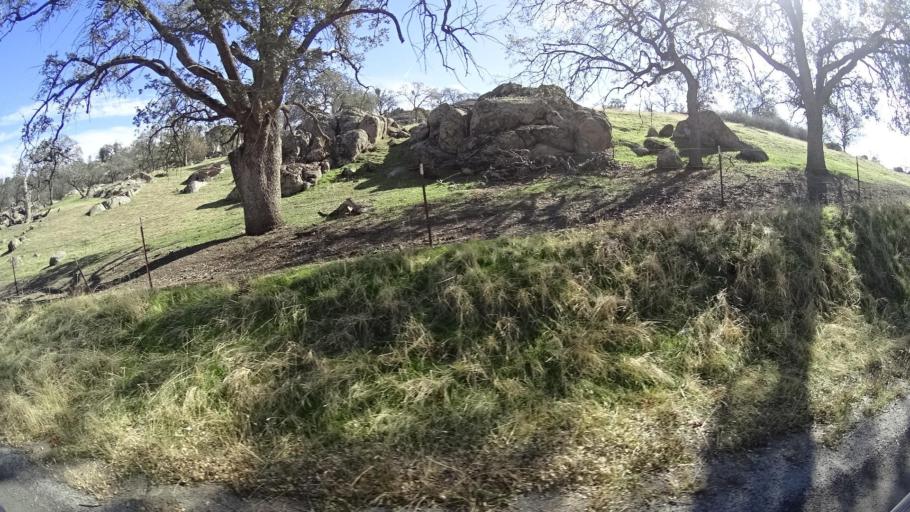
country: US
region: California
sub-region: Kern County
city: Oildale
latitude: 35.6272
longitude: -118.8452
